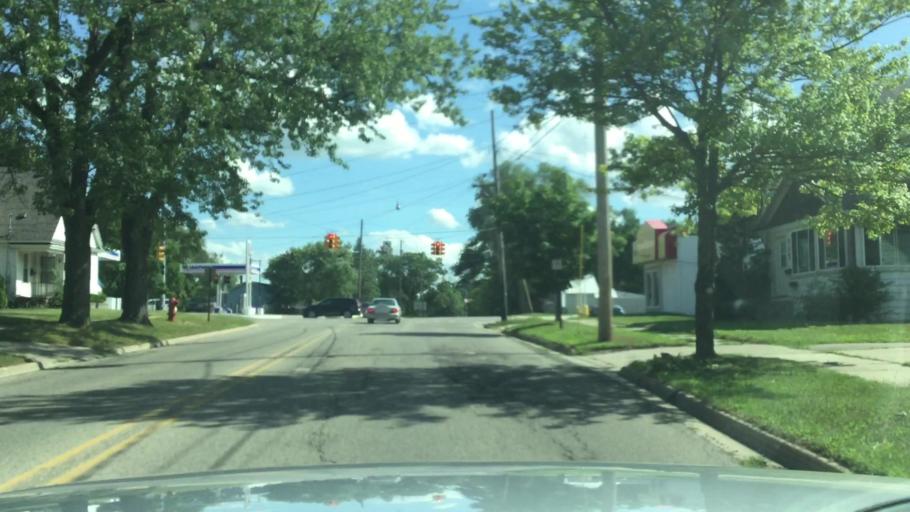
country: US
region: Michigan
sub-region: Ionia County
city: Belding
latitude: 43.0896
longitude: -85.2288
